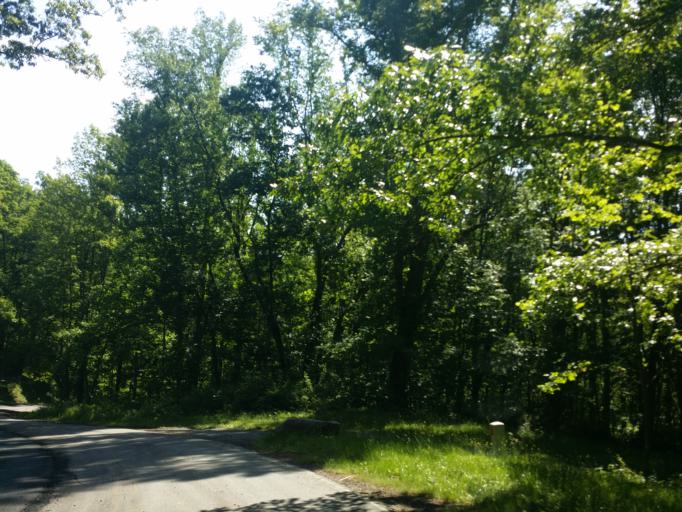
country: US
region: North Carolina
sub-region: Haywood County
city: Cove Creek
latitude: 35.7729
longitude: -82.8934
